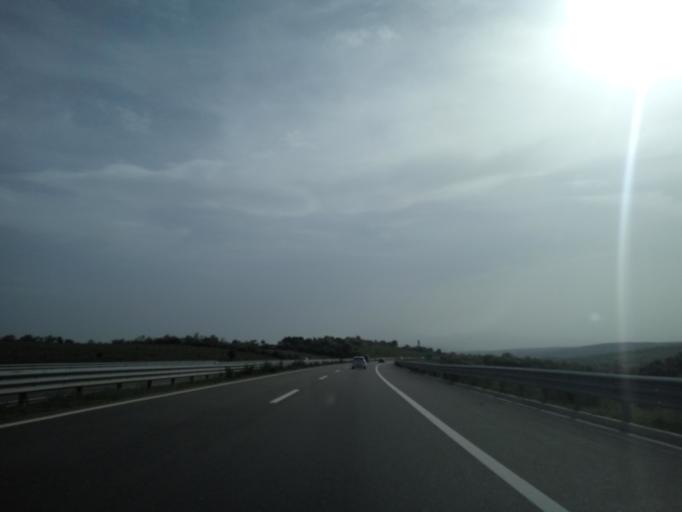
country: XK
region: Prizren
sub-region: Komuna e Therandes
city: Peqan
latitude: 42.3742
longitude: 20.8400
